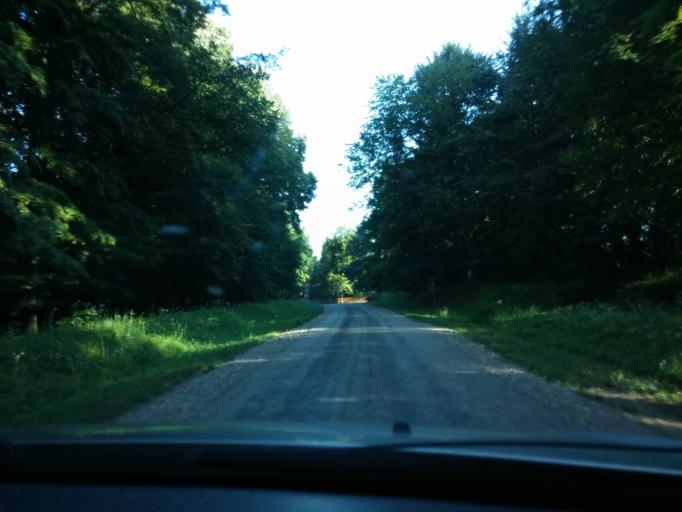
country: HU
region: Somogy
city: Kaposmero
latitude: 46.2449
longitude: 17.7576
